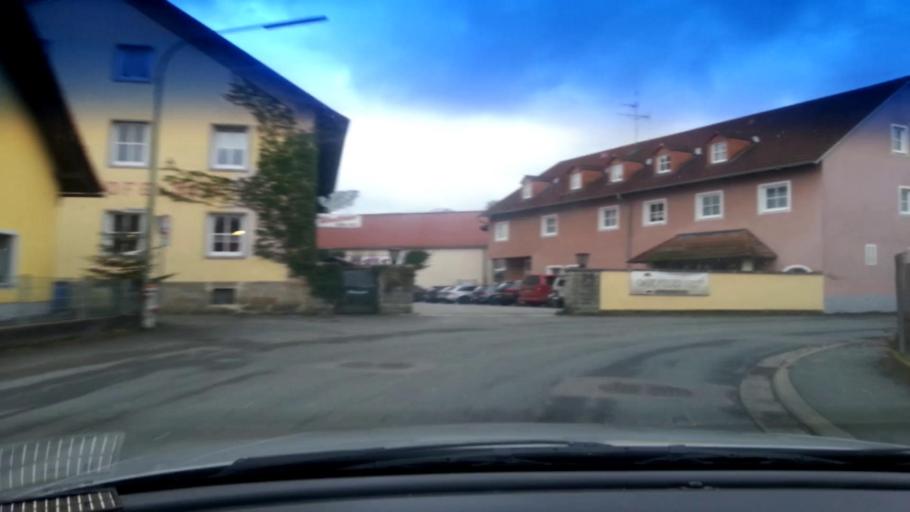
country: DE
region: Bavaria
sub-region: Upper Franconia
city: Stegaurach
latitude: 49.8625
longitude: 10.8428
